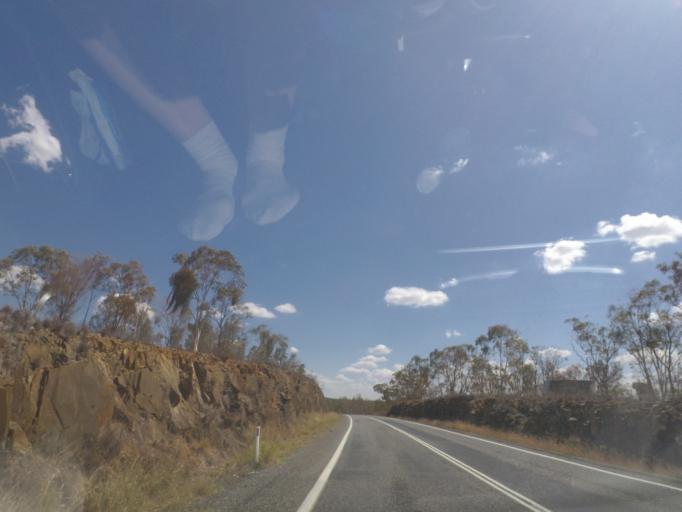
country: AU
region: Queensland
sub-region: Southern Downs
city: Warwick
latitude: -28.2096
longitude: 151.5653
